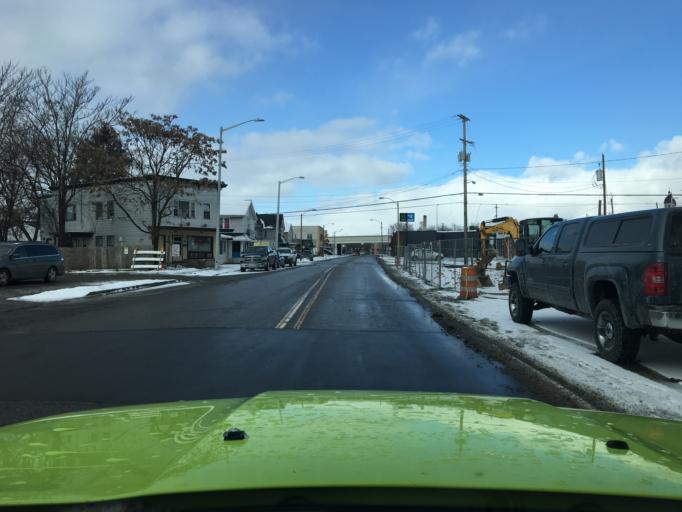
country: US
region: Michigan
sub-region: Kent County
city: Grand Rapids
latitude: 42.9714
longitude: -85.6845
